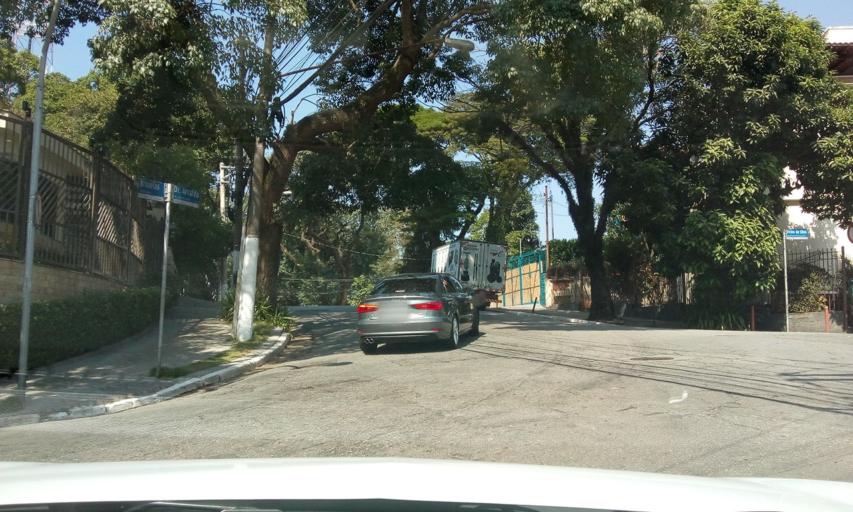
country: BR
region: Sao Paulo
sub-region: Sao Paulo
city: Sao Paulo
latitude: -23.5438
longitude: -46.6835
